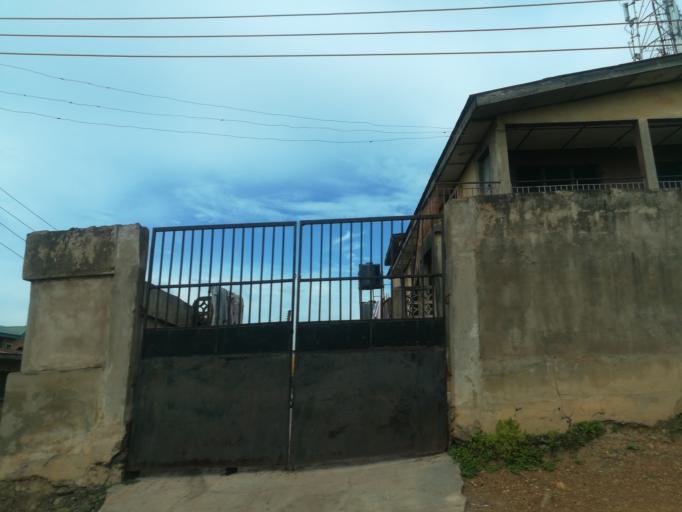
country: NG
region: Oyo
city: Ibadan
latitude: 7.3831
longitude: 3.9424
